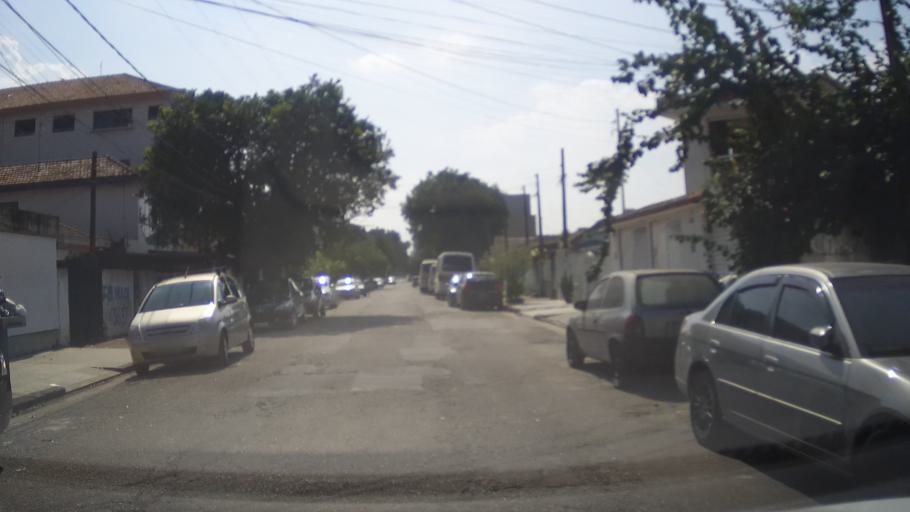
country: BR
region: Sao Paulo
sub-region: Santos
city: Santos
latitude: -23.9750
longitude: -46.2983
